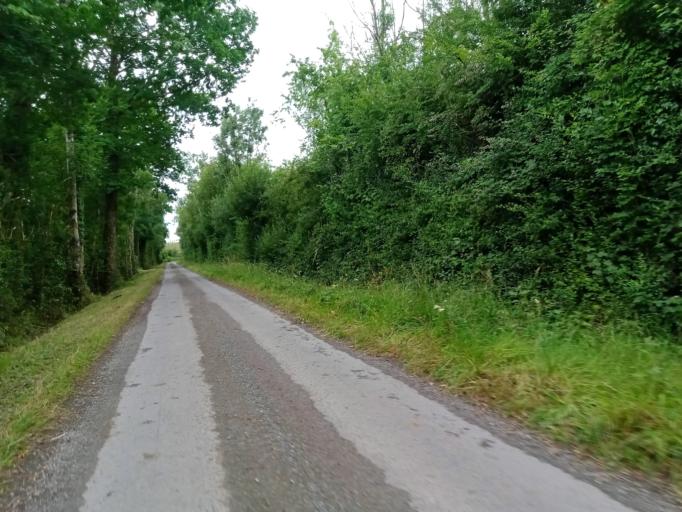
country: IE
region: Leinster
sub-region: Kilkenny
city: Callan
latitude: 52.5797
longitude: -7.4028
